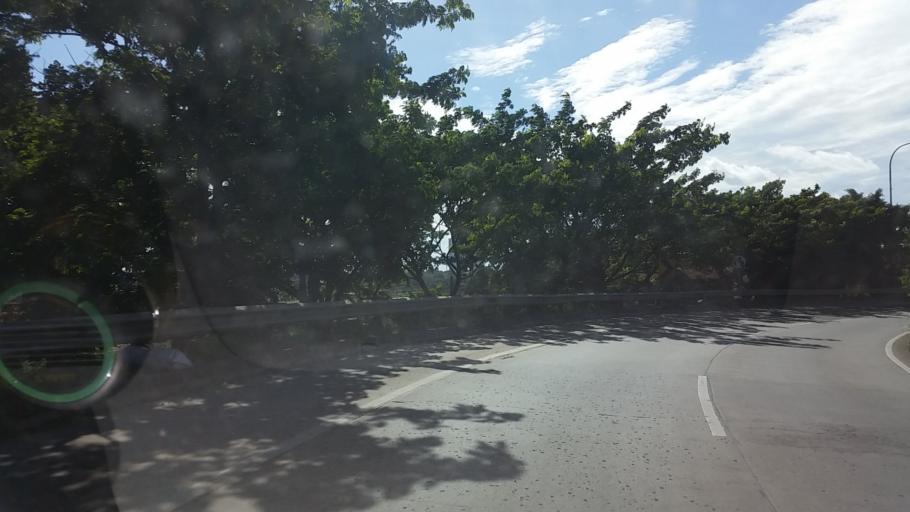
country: ID
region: Banten
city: South Tangerang
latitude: -6.2504
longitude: 106.7641
